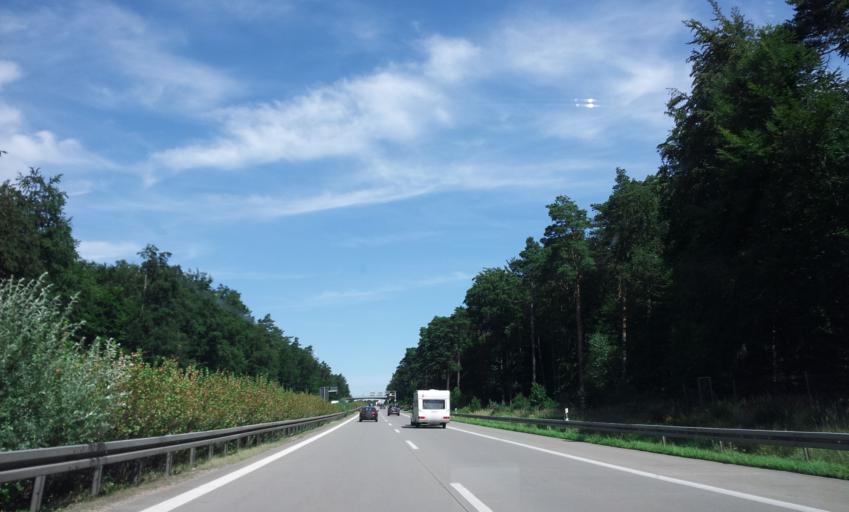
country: DE
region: Brandenburg
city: Bernau bei Berlin
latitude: 52.7374
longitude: 13.5409
